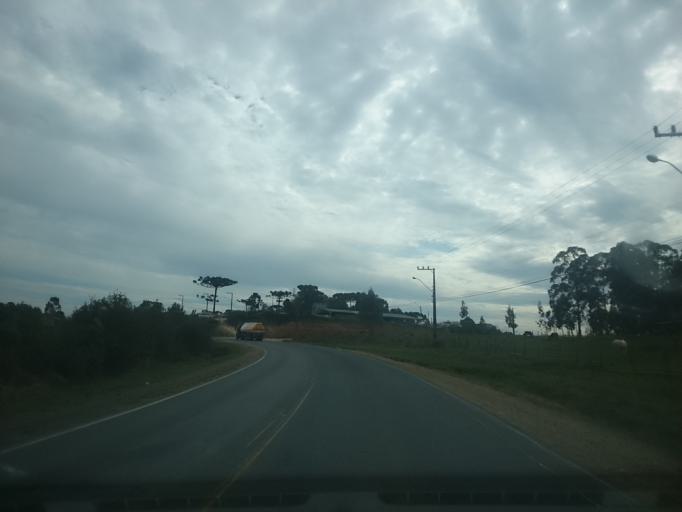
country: BR
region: Santa Catarina
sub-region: Lages
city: Lages
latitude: -27.7756
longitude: -50.3195
